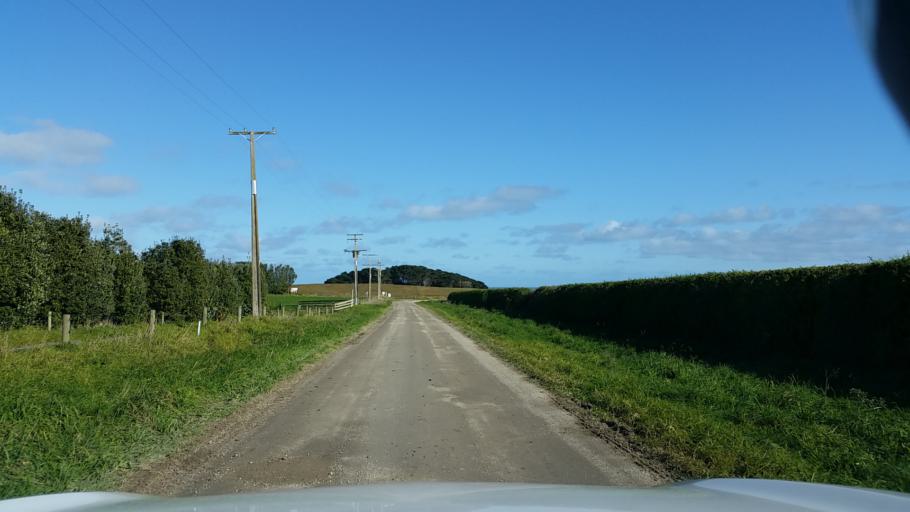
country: NZ
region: Taranaki
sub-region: South Taranaki District
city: Patea
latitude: -39.6858
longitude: 174.3981
